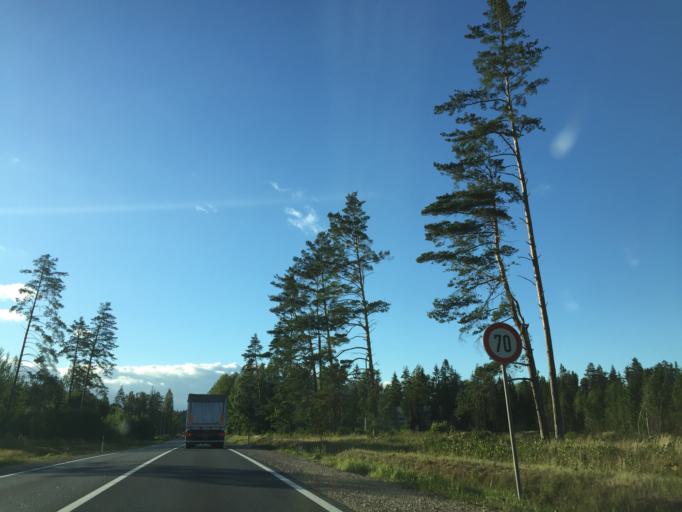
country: LV
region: Jekabpils Rajons
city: Jekabpils
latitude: 56.5362
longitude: 25.8177
